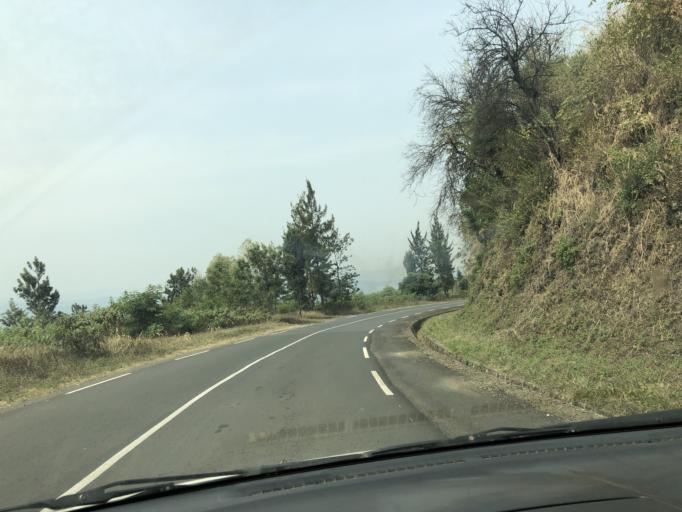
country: RW
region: Western Province
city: Cyangugu
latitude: -2.6675
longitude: 29.0014
